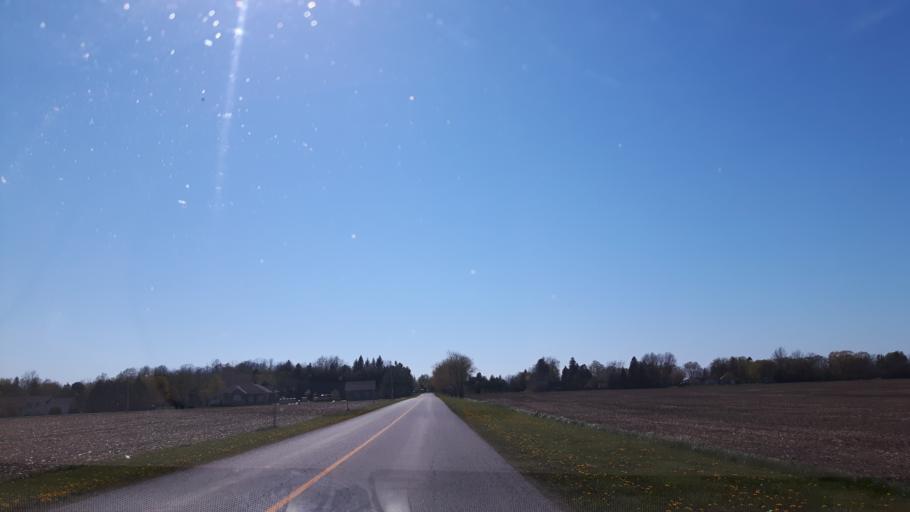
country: CA
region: Ontario
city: Bluewater
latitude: 43.5108
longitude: -81.7042
